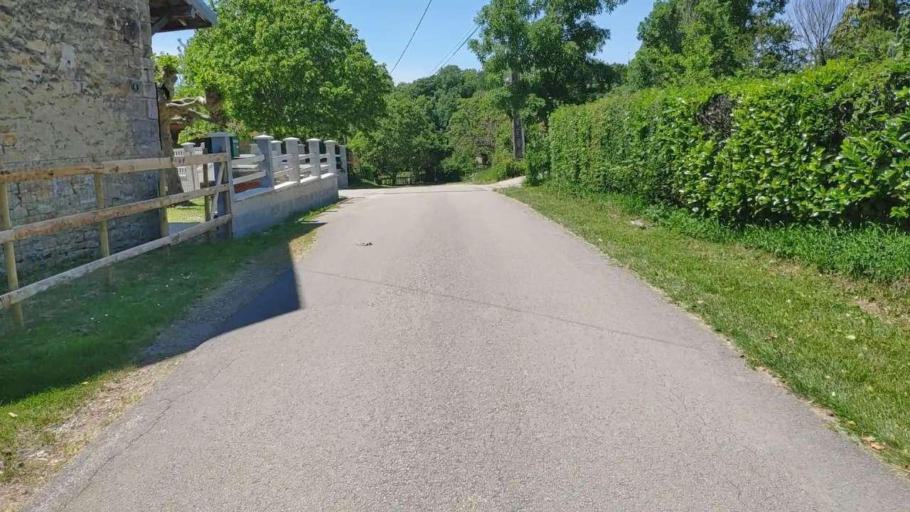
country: FR
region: Franche-Comte
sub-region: Departement du Jura
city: Bletterans
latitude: 46.7389
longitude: 5.4294
